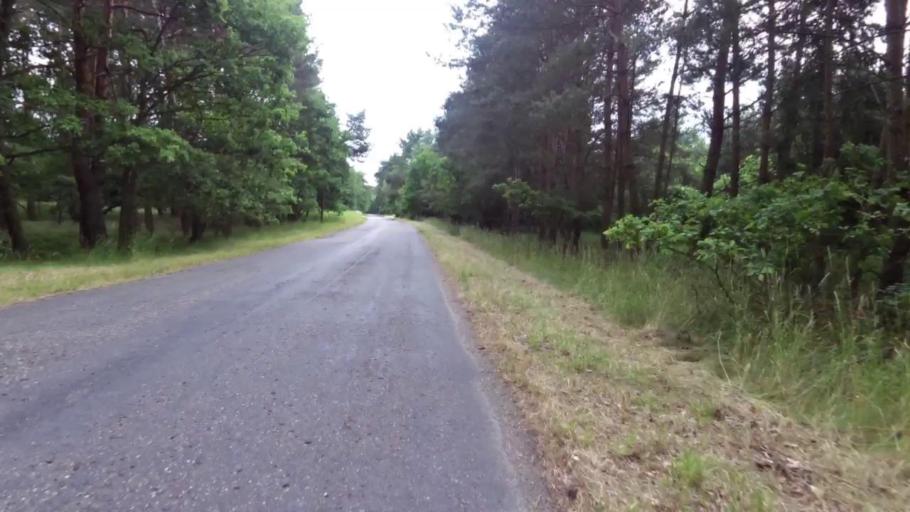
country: PL
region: West Pomeranian Voivodeship
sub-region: Powiat goleniowski
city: Stepnica
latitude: 53.7088
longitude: 14.5515
